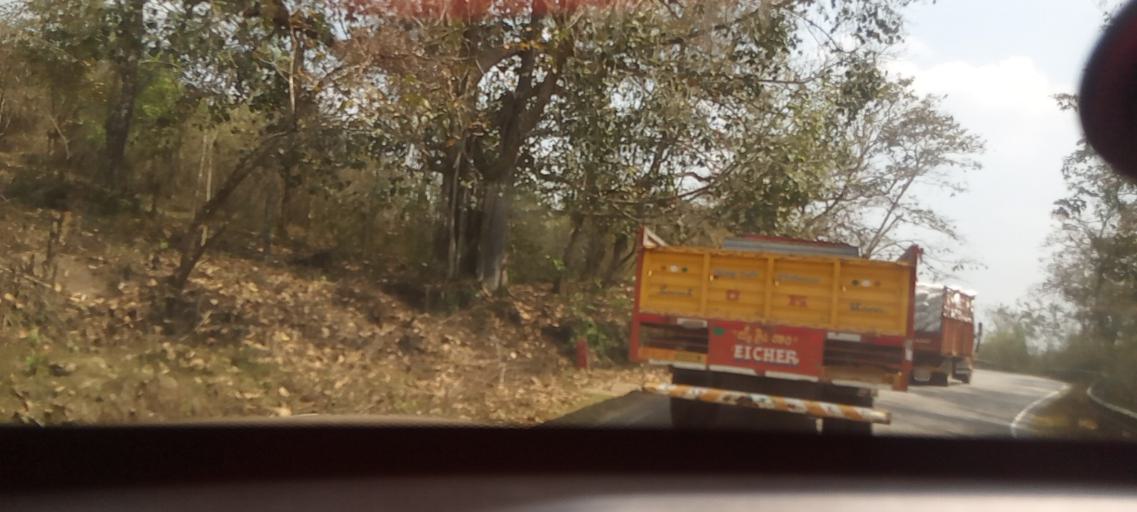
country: IN
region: Karnataka
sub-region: Chikmagalur
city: Mudigere
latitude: 13.3005
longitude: 75.5891
